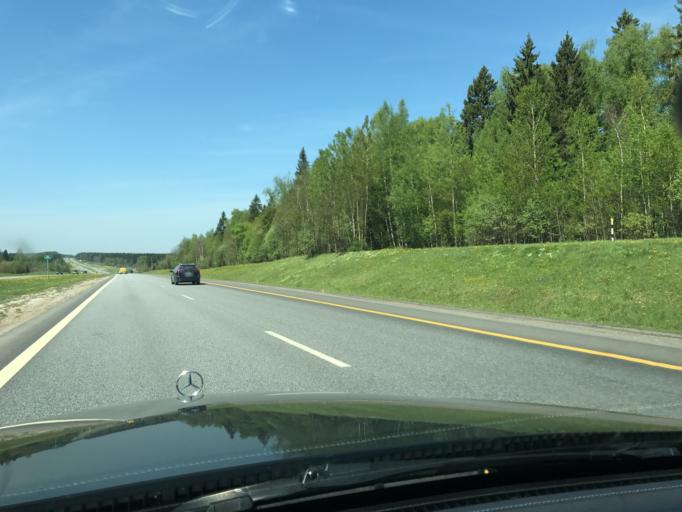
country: RU
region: Moskovskaya
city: Novopetrovskoye
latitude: 55.9836
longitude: 36.3548
